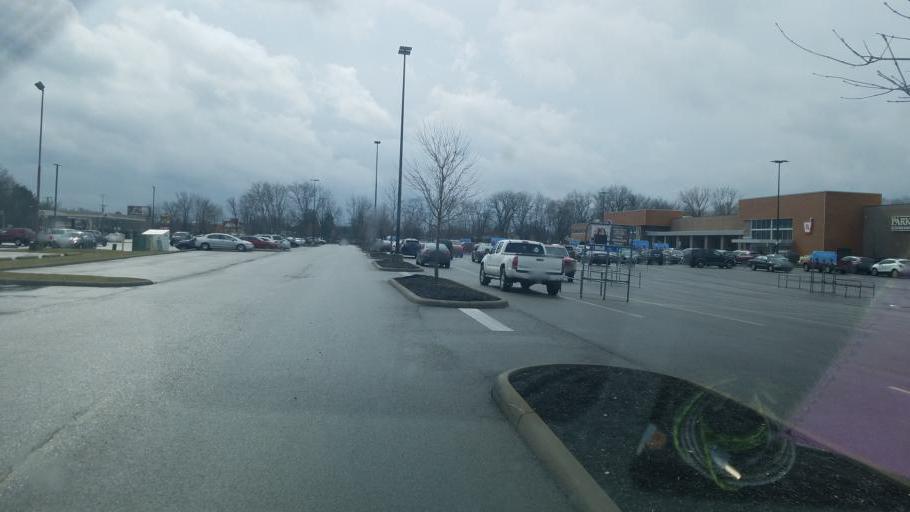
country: US
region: Ohio
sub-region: Licking County
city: Newark
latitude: 40.0812
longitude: -82.4291
